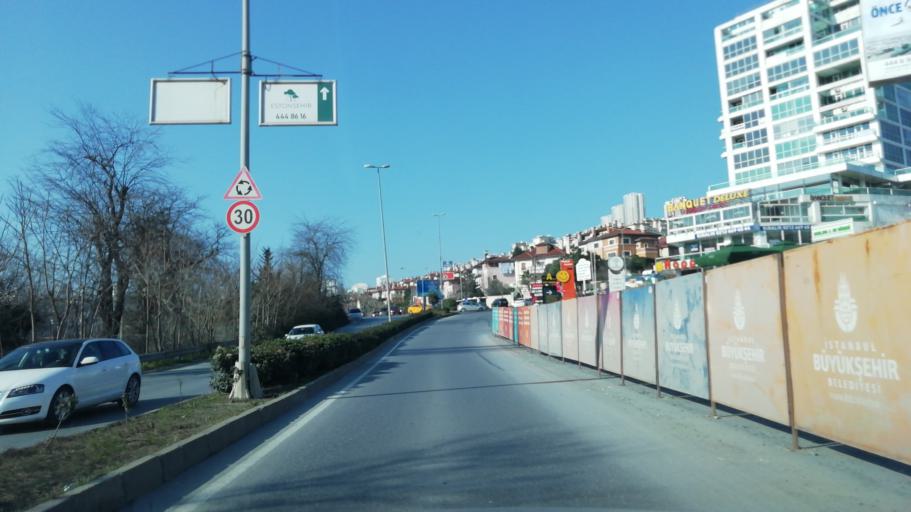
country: TR
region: Istanbul
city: Esenyurt
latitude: 41.0636
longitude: 28.6997
